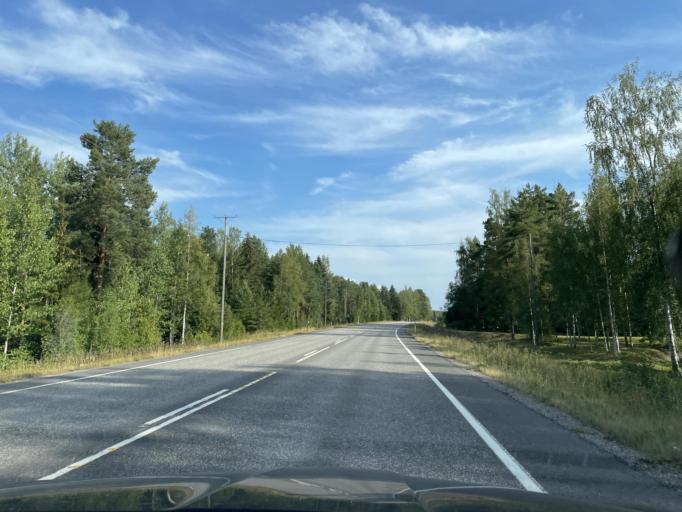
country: FI
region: Central Finland
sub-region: Jaemsae
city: Jaemsae
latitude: 61.7597
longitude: 25.2513
